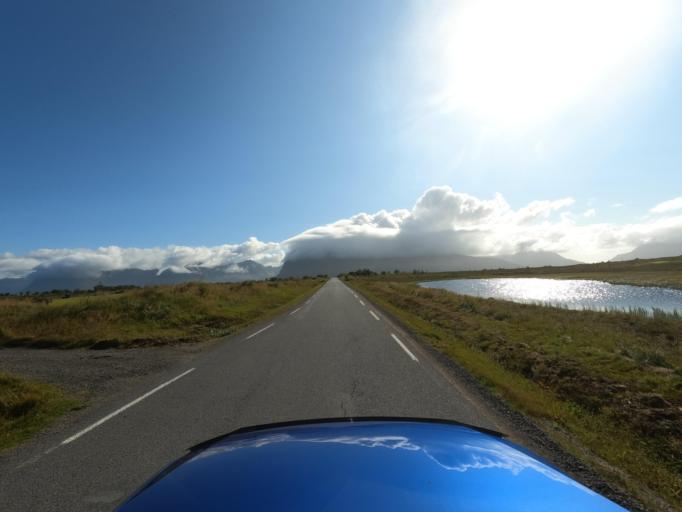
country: NO
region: Nordland
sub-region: Vagan
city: Kabelvag
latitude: 68.3406
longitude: 14.1395
